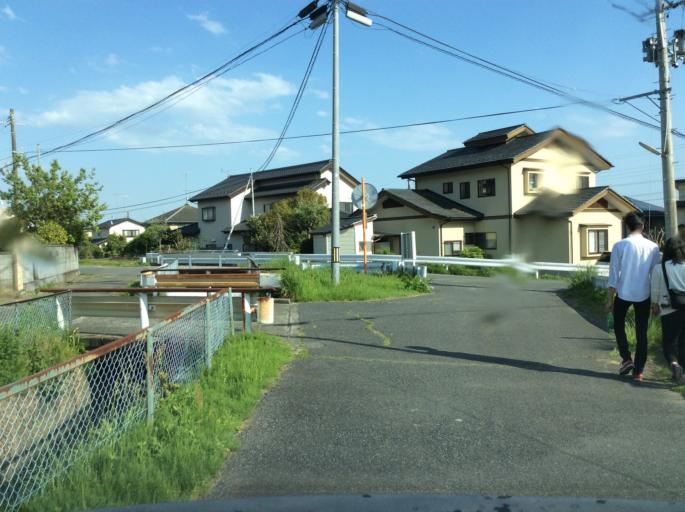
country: JP
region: Fukushima
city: Iwaki
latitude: 36.9605
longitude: 140.8560
